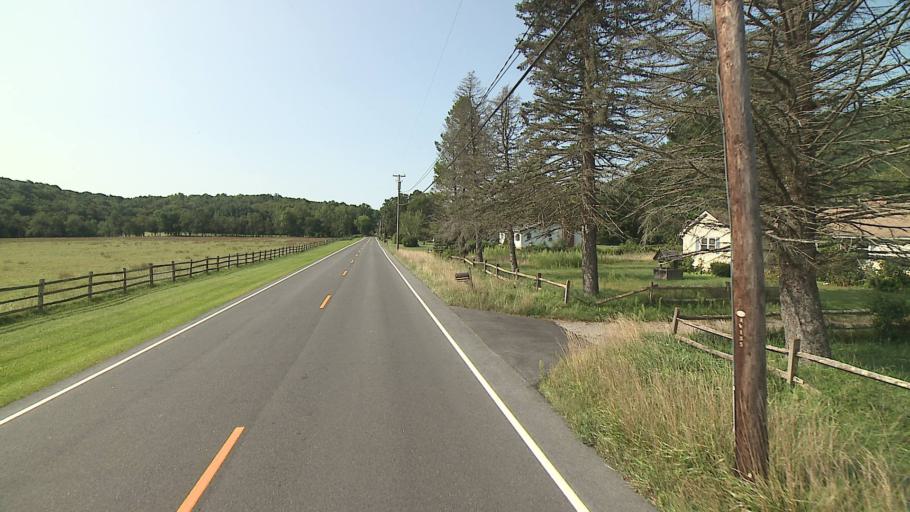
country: US
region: Connecticut
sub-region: Litchfield County
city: Kent
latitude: 41.7051
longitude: -73.4902
